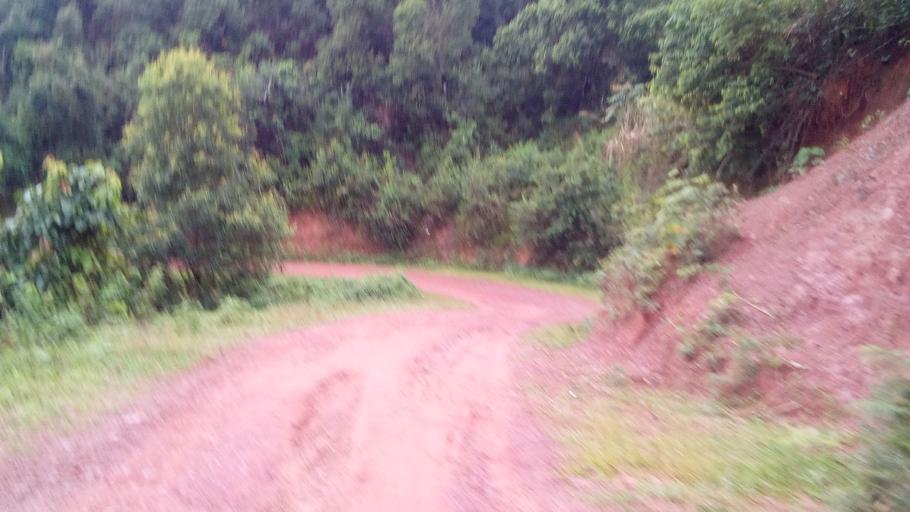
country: TH
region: Nan
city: Chaloem Phra Kiat
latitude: 19.4334
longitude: 101.2402
